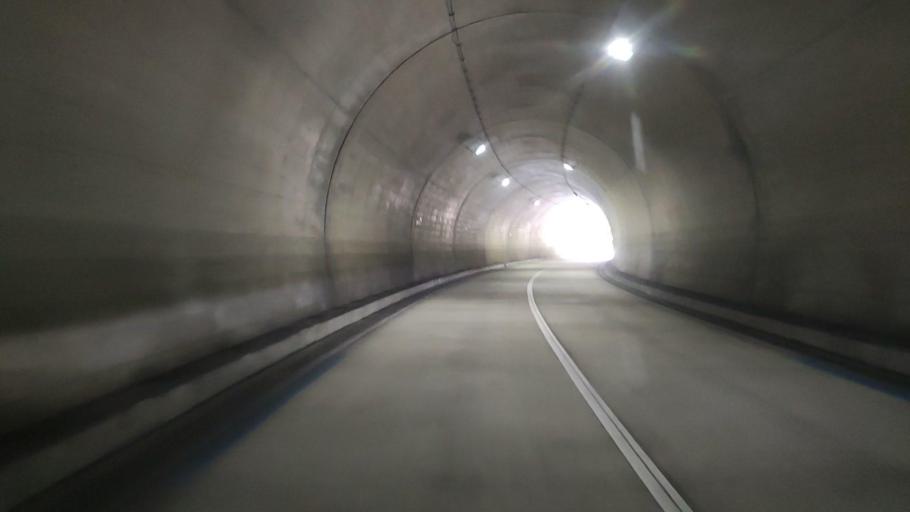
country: JP
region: Wakayama
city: Shingu
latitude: 33.8728
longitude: 135.8557
